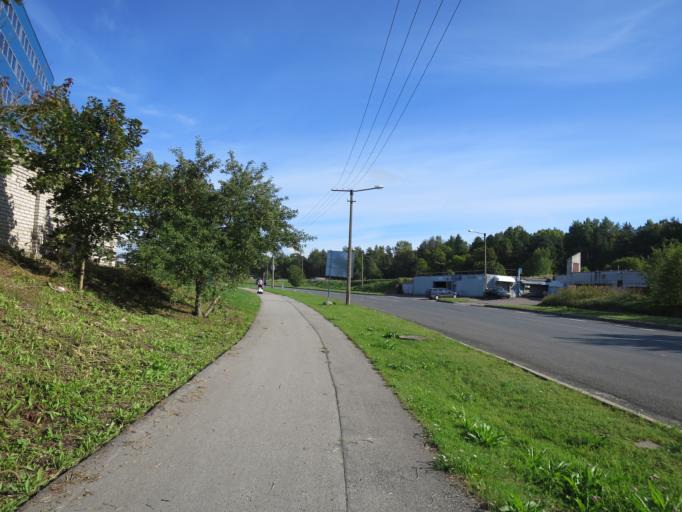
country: EE
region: Harju
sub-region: Tallinna linn
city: Tallinn
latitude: 59.3953
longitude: 24.7039
